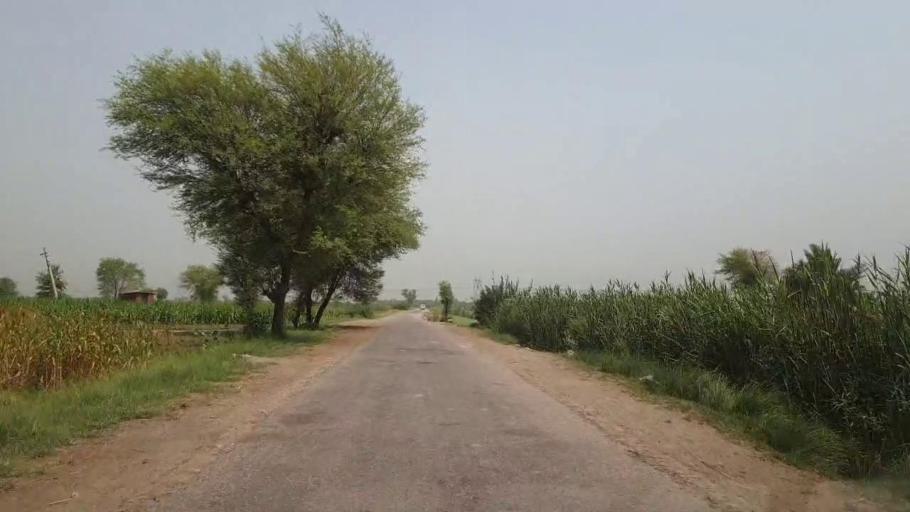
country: PK
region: Sindh
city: Gambat
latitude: 27.4078
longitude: 68.5504
